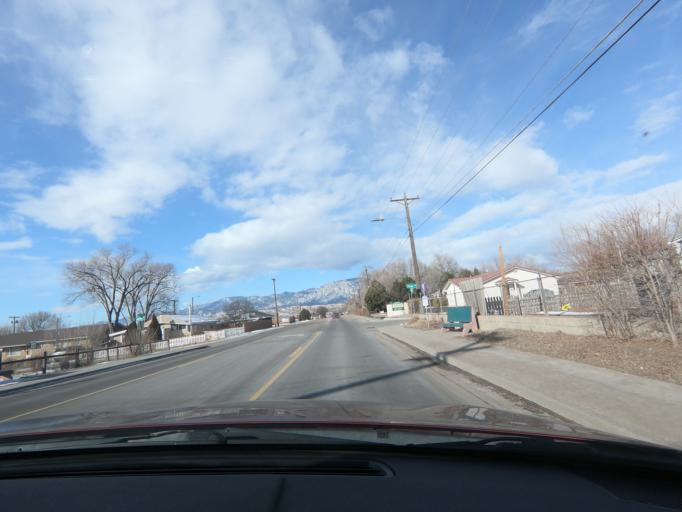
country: US
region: Colorado
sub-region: El Paso County
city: Security-Widefield
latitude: 38.7374
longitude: -104.7243
